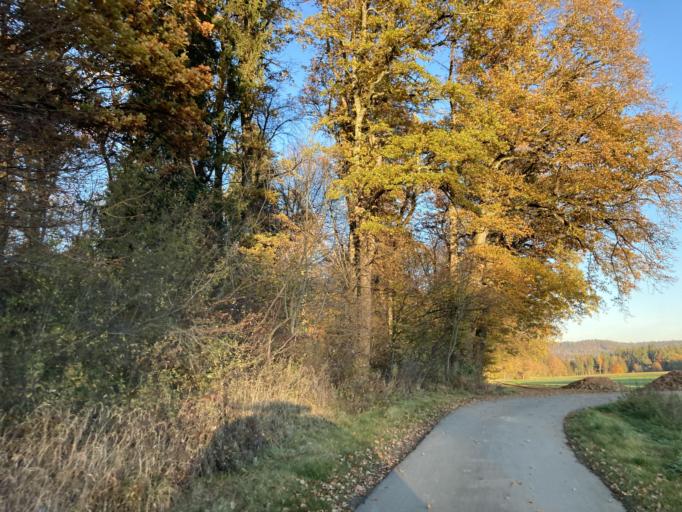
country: DE
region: Baden-Wuerttemberg
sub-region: Tuebingen Region
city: Hirrlingen
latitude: 48.4381
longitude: 8.8966
